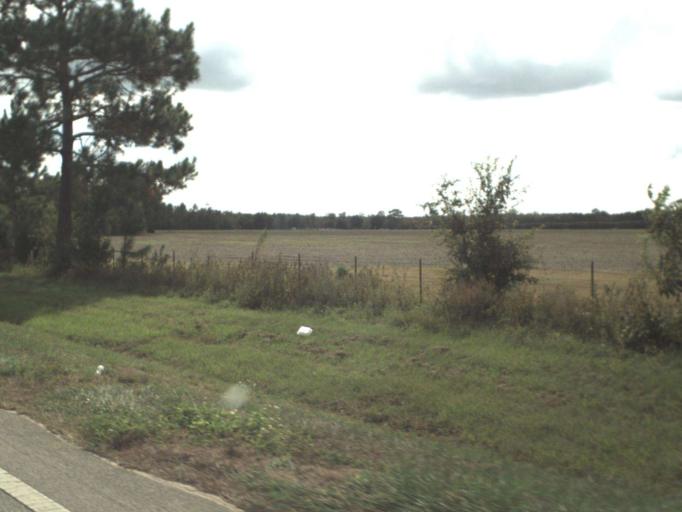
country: US
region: Florida
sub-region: Gadsden County
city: Gretna
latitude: 30.6963
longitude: -84.6240
